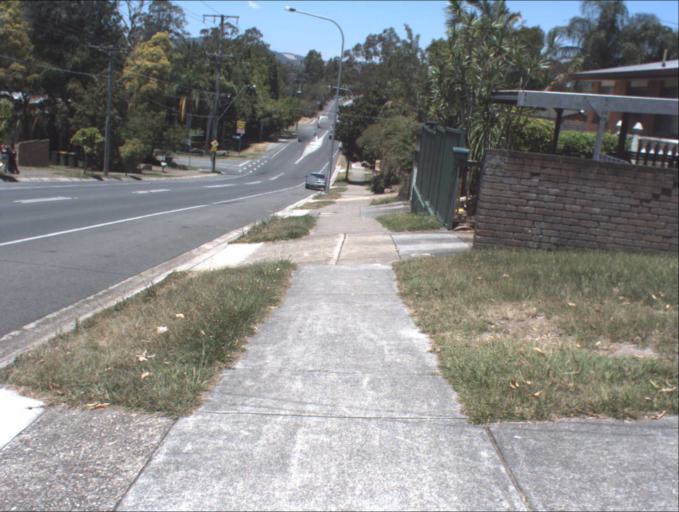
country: AU
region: Queensland
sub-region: Gold Coast
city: Yatala
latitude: -27.7122
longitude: 153.2112
